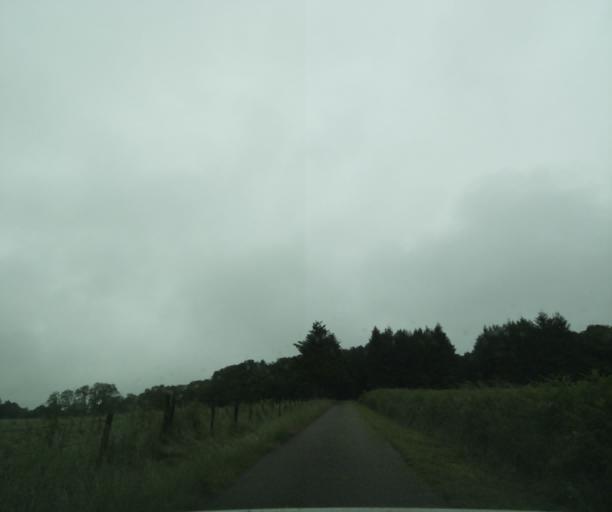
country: FR
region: Bourgogne
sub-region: Departement de Saone-et-Loire
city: Charolles
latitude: 46.4380
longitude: 4.3698
